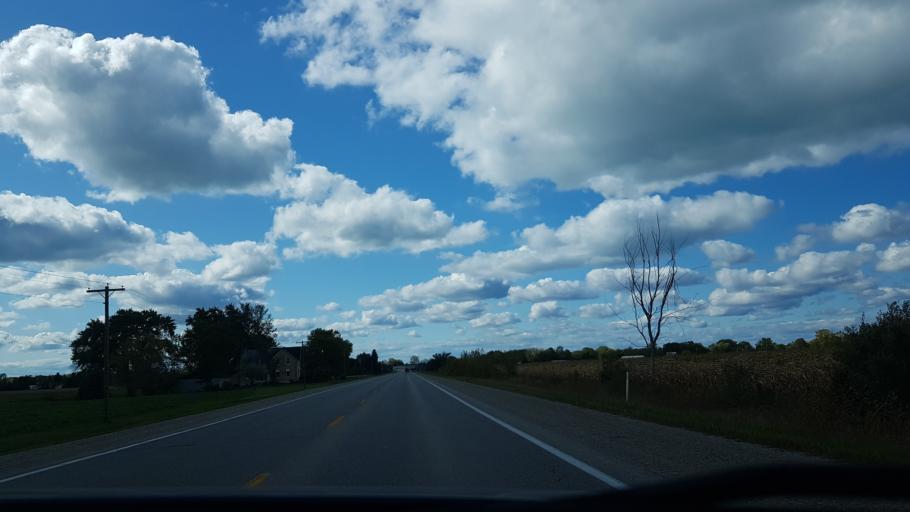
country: CA
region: Ontario
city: Bluewater
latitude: 43.3365
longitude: -81.7268
